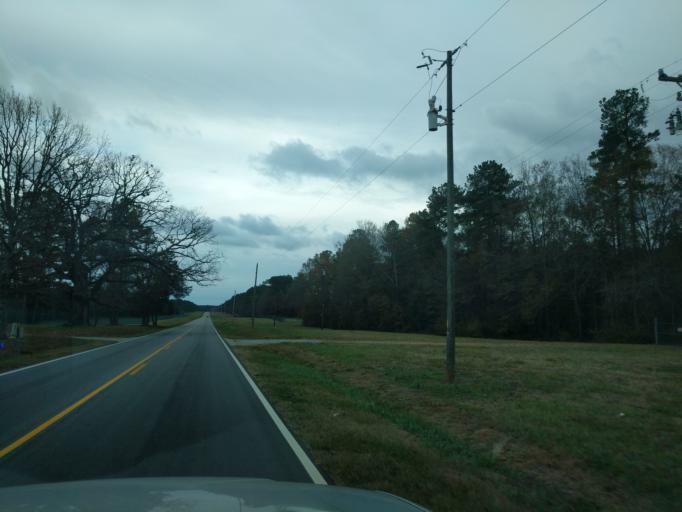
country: US
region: South Carolina
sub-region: Laurens County
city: Laurens
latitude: 34.4170
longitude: -82.0431
